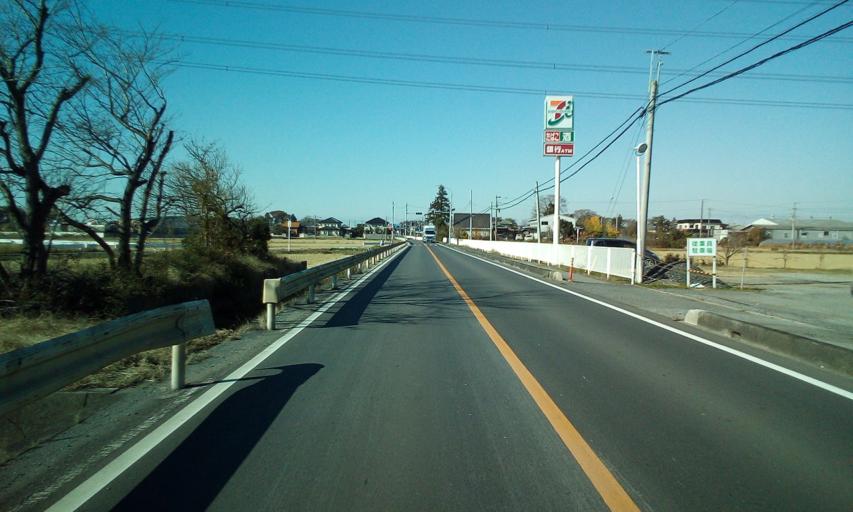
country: JP
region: Saitama
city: Sugito
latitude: 36.0509
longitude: 139.7768
